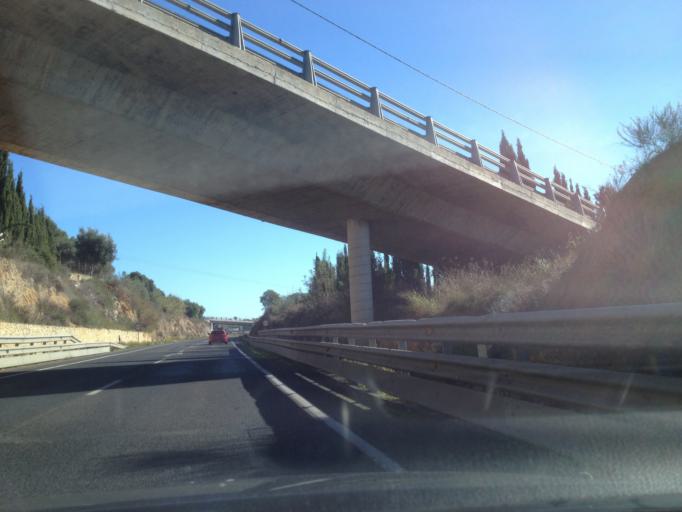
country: ES
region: Balearic Islands
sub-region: Illes Balears
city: Manacor
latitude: 39.5864
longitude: 3.2244
